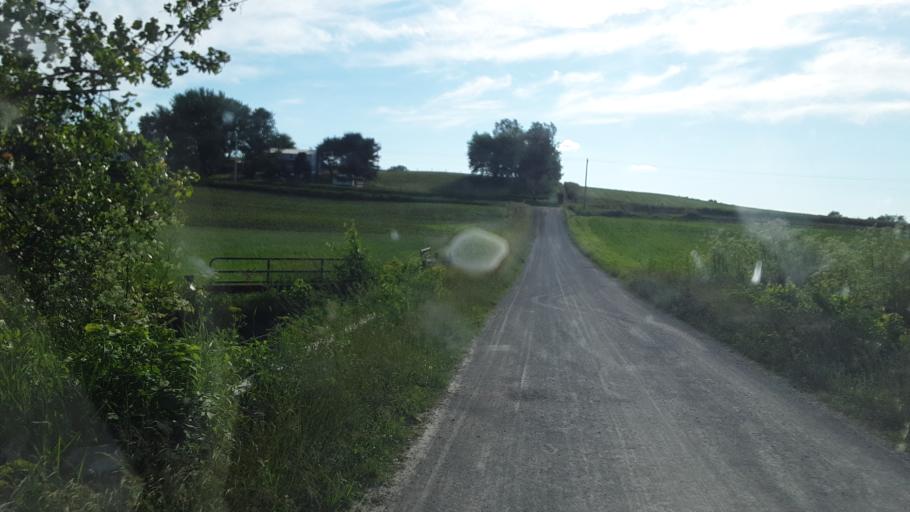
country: US
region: Ohio
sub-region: Wayne County
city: Apple Creek
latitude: 40.6527
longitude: -81.8592
